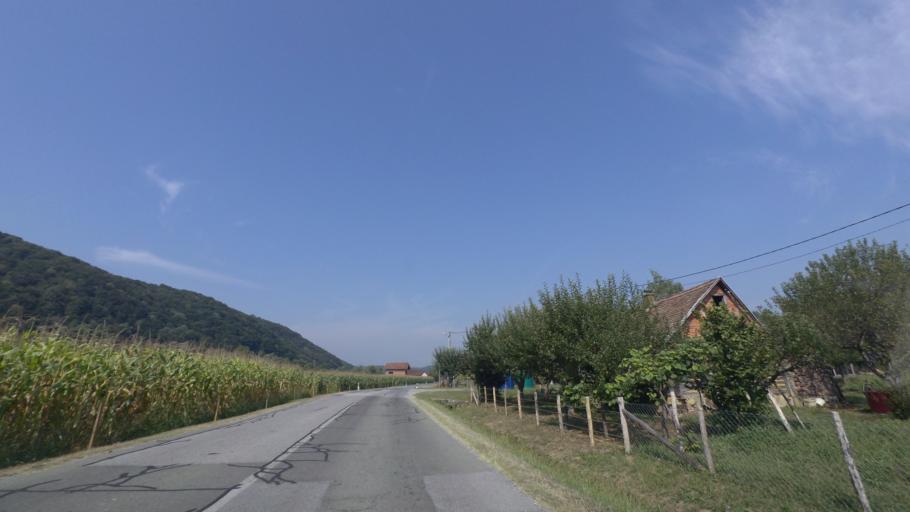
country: HR
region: Sisacko-Moslavacka
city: Dvor
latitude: 45.0747
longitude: 16.3526
